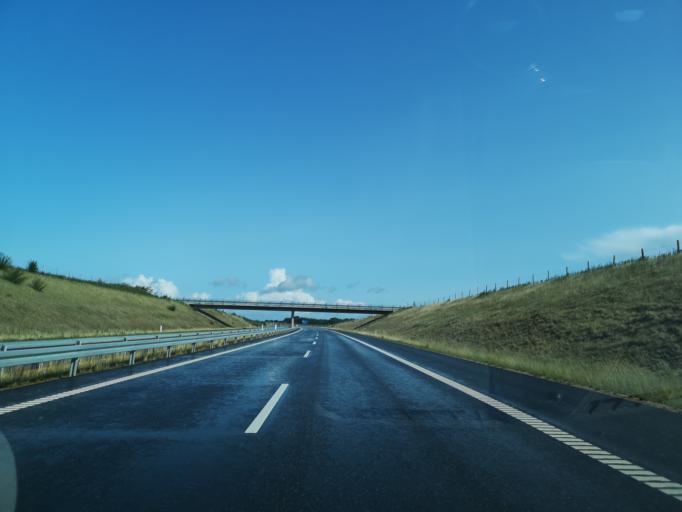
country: DK
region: Central Jutland
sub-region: Herning Kommune
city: Snejbjerg
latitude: 56.1732
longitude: 8.8917
